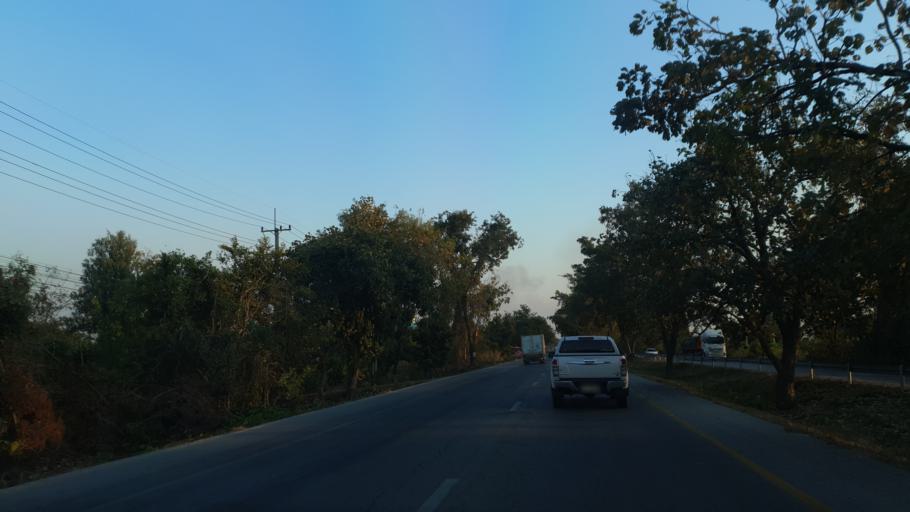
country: TH
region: Nakhon Sawan
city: Banphot Phisai
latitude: 15.8929
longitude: 99.8990
